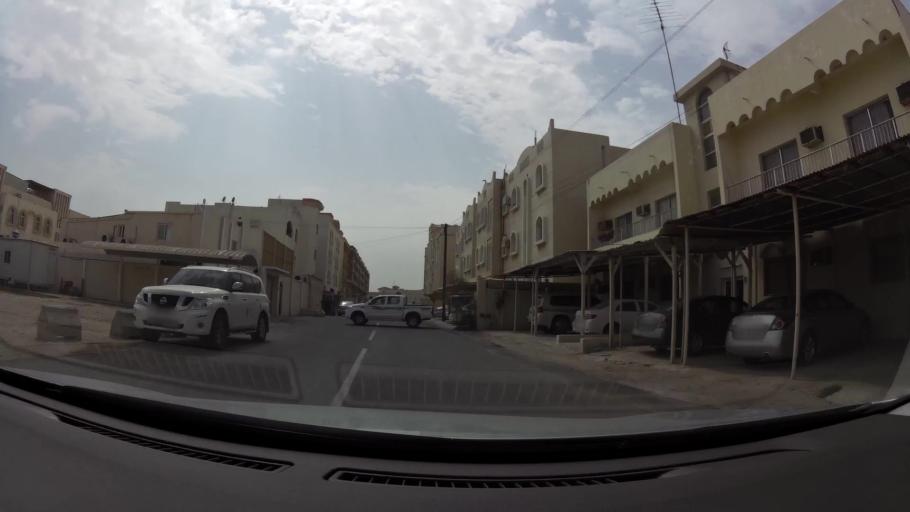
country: QA
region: Baladiyat ad Dawhah
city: Doha
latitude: 25.3096
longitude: 51.4956
